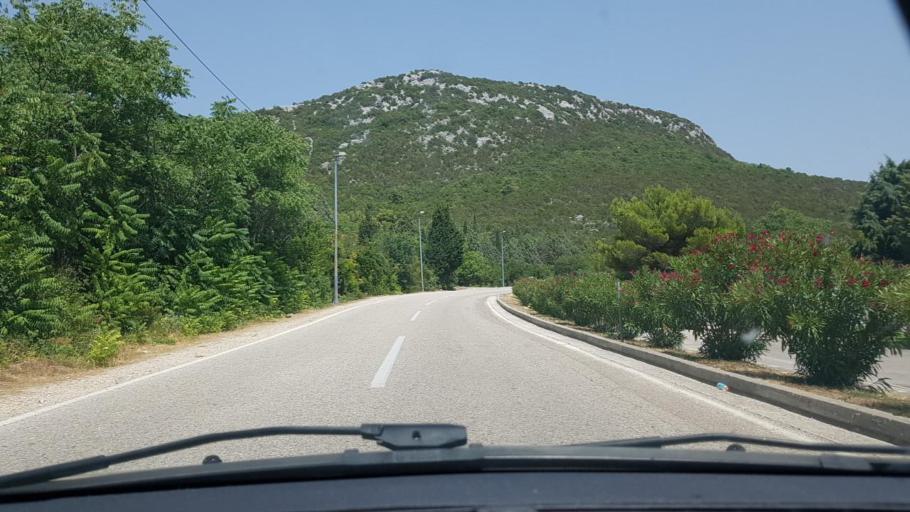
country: BA
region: Federation of Bosnia and Herzegovina
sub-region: Hercegovacko-Bosanski Kanton
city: Neum
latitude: 42.9266
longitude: 17.6278
